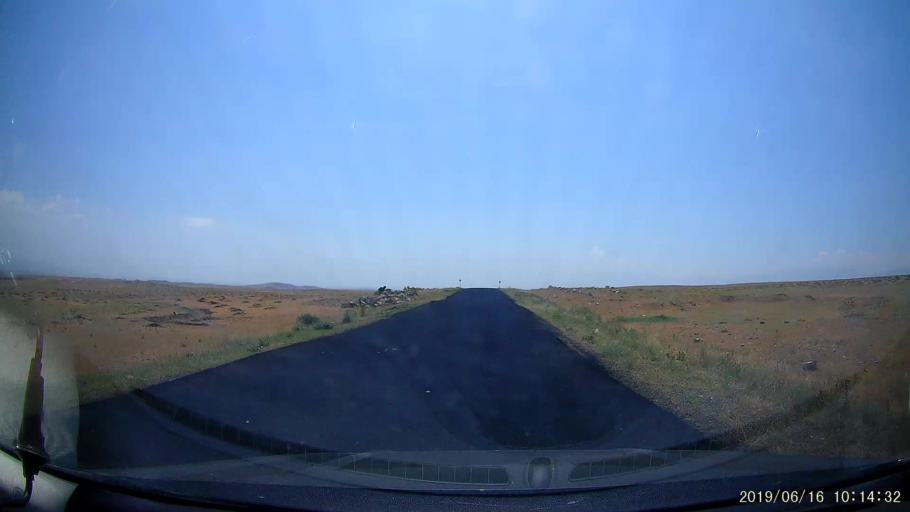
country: TR
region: Igdir
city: Tuzluca
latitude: 40.1839
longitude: 43.6648
